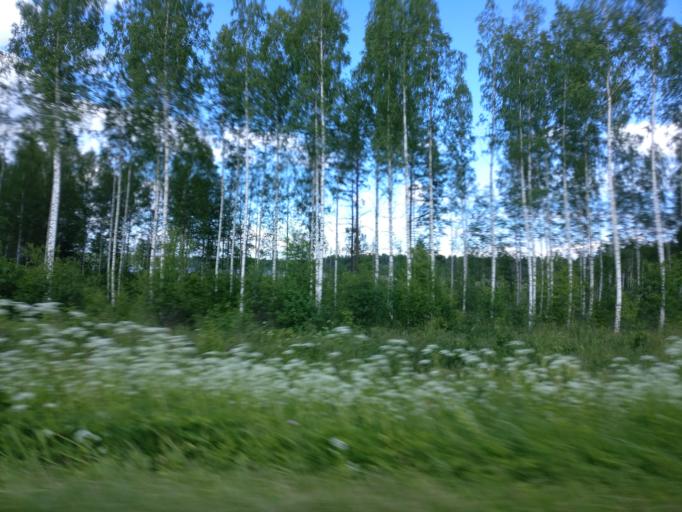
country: FI
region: Southern Savonia
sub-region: Savonlinna
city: Kerimaeki
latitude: 61.8397
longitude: 29.2154
